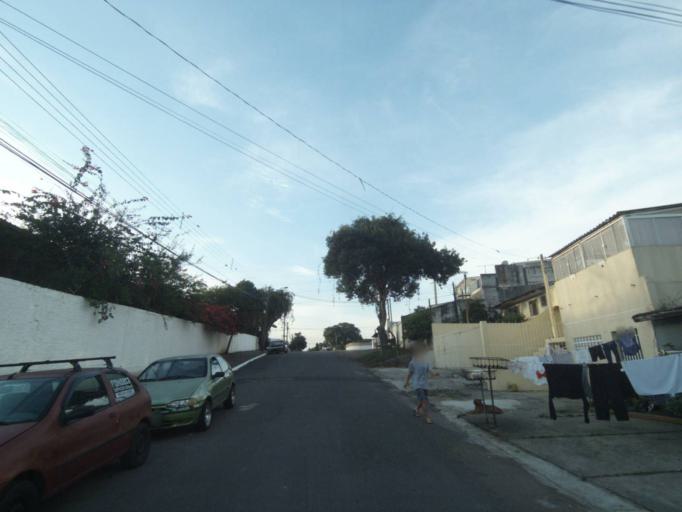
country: BR
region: Parana
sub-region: Curitiba
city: Curitiba
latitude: -25.4658
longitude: -49.3082
